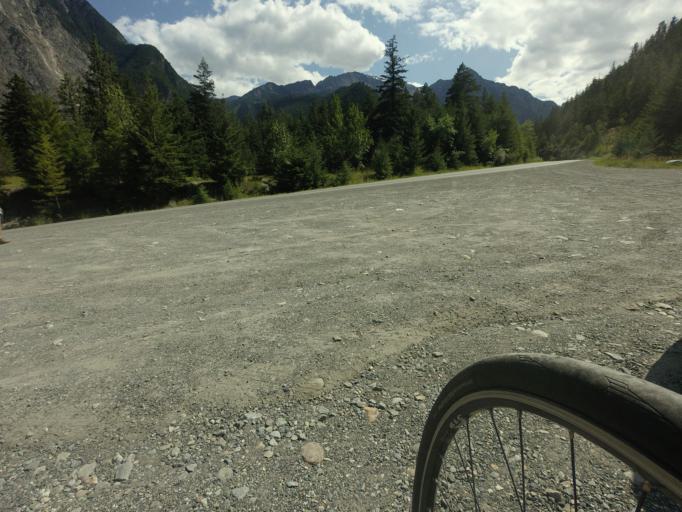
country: CA
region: British Columbia
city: Lillooet
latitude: 50.6625
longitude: -121.9908
